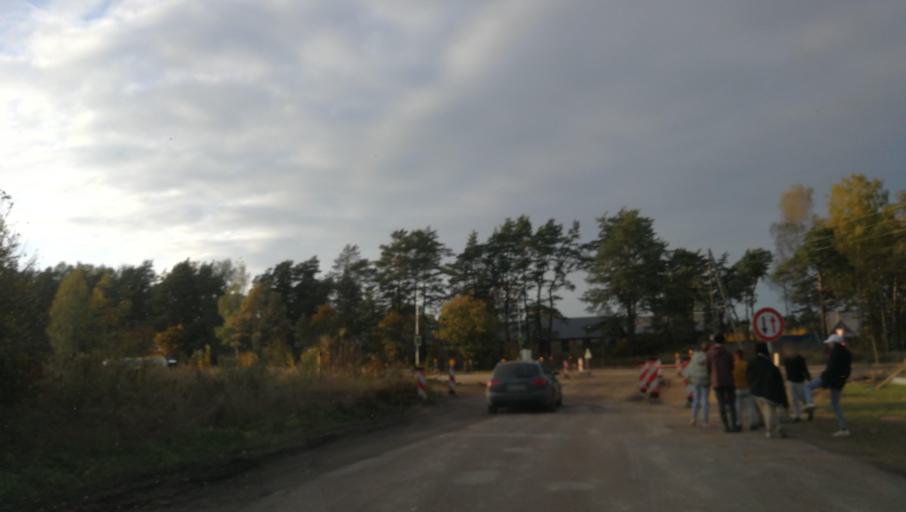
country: LV
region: Incukalns
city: Incukalns
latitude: 57.1264
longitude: 24.7039
